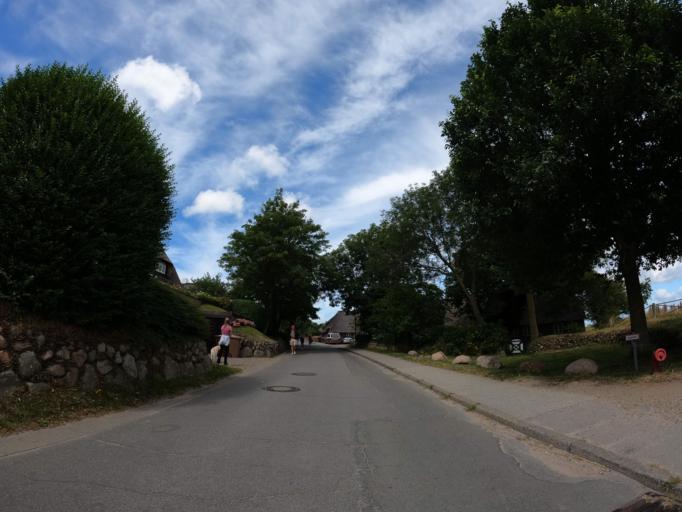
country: DE
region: Schleswig-Holstein
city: Keitum
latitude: 54.8983
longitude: 8.3682
